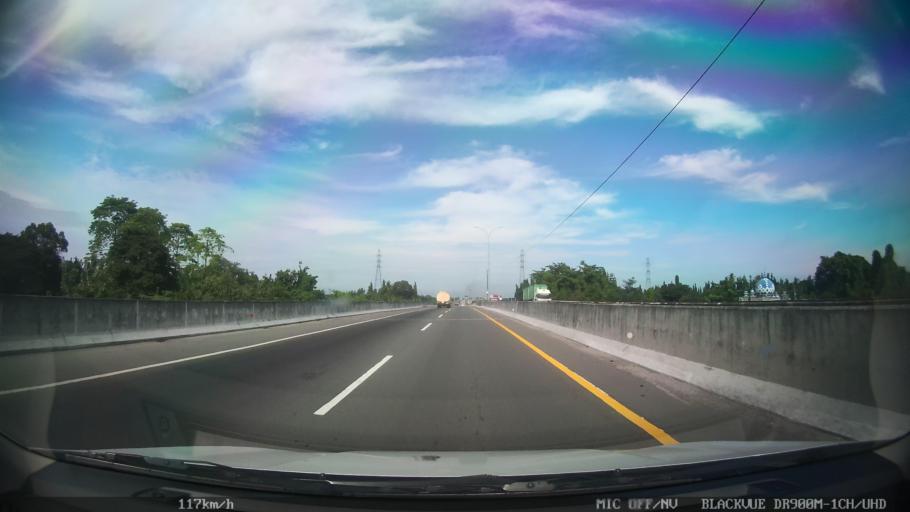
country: ID
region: North Sumatra
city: Sunggal
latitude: 3.6375
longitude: 98.5941
